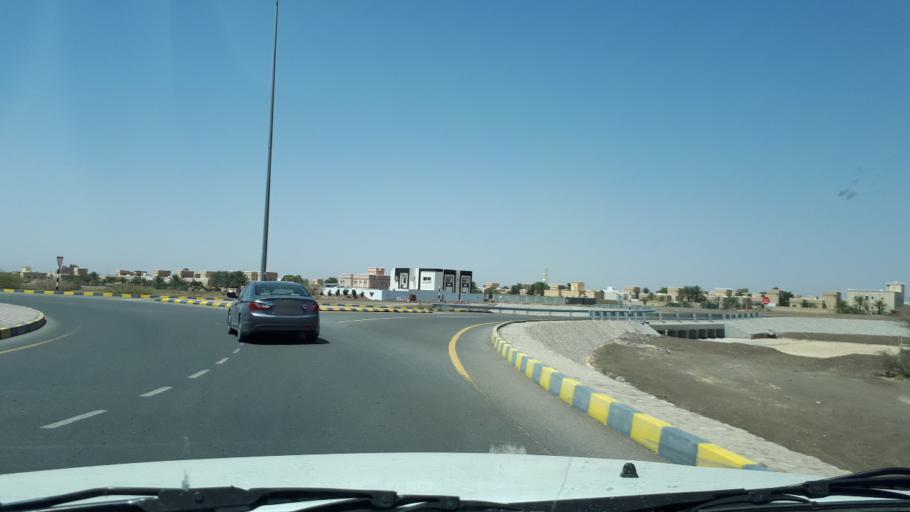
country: OM
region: Muhafazat ad Dakhiliyah
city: Bahla'
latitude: 22.9255
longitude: 57.2561
